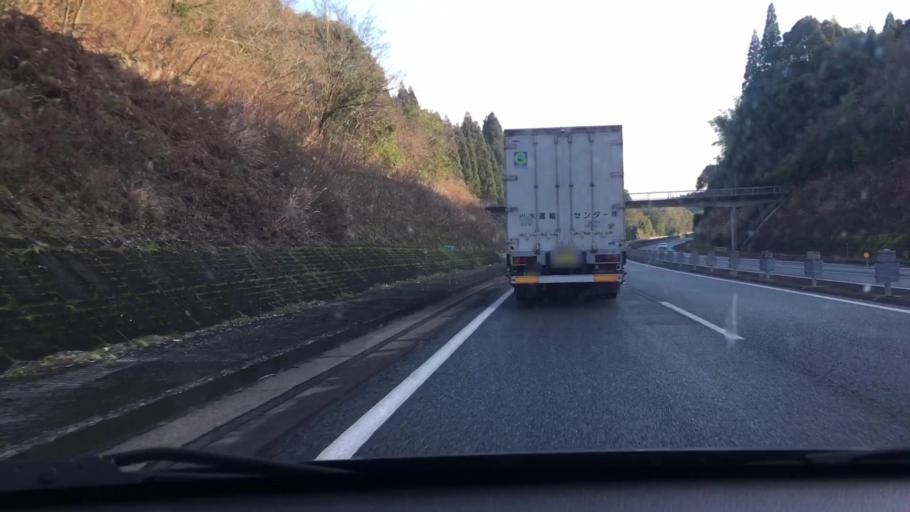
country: JP
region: Kagoshima
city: Okuchi-shinohara
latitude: 31.9096
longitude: 130.7061
